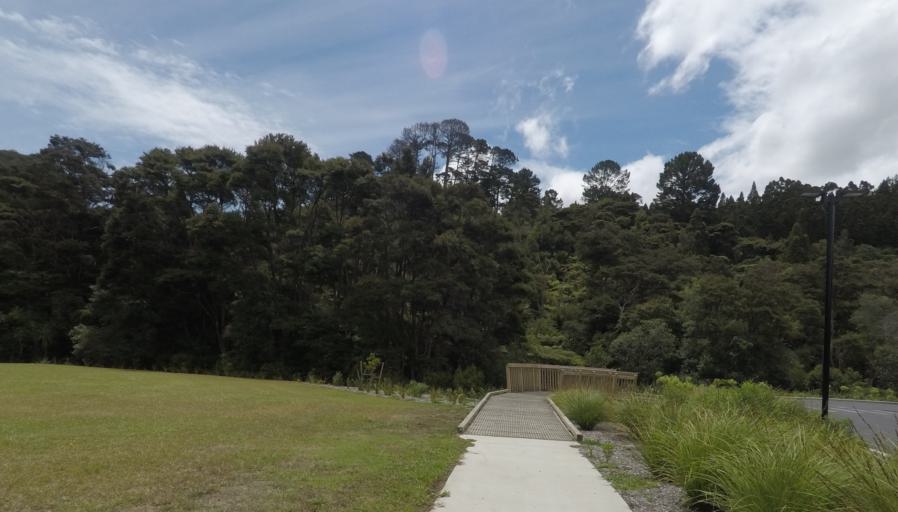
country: NZ
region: Auckland
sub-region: Auckland
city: Rosebank
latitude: -36.8627
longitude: 174.5902
